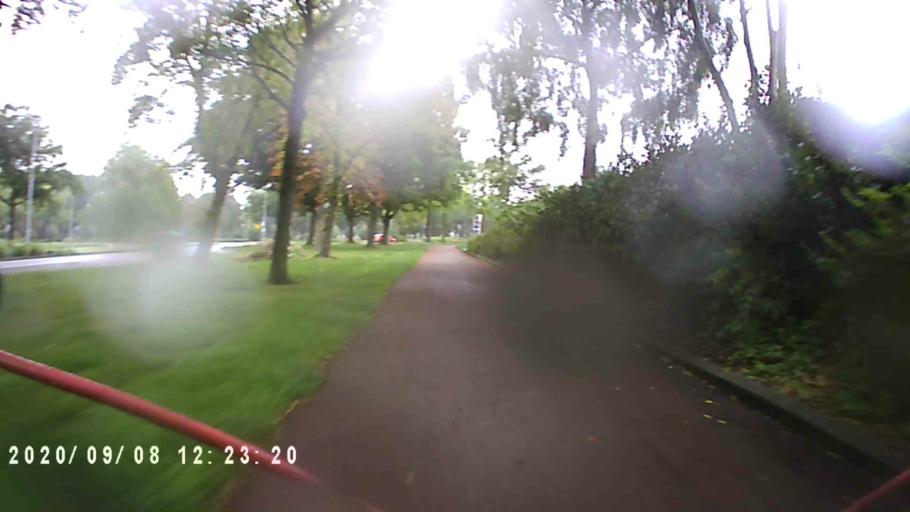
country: NL
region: Groningen
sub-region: Gemeente Veendam
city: Veendam
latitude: 53.0952
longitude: 6.8572
